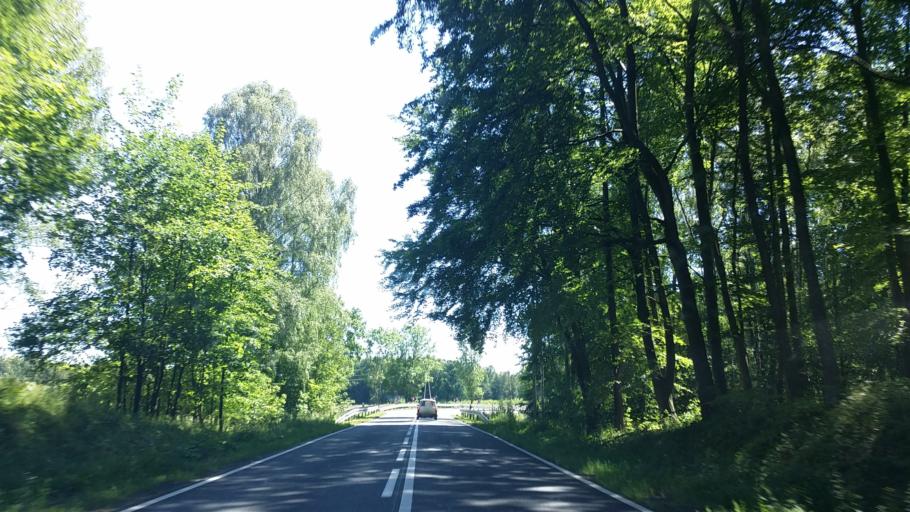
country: PL
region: West Pomeranian Voivodeship
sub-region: Powiat stargardzki
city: Insko
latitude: 53.4817
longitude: 15.5814
